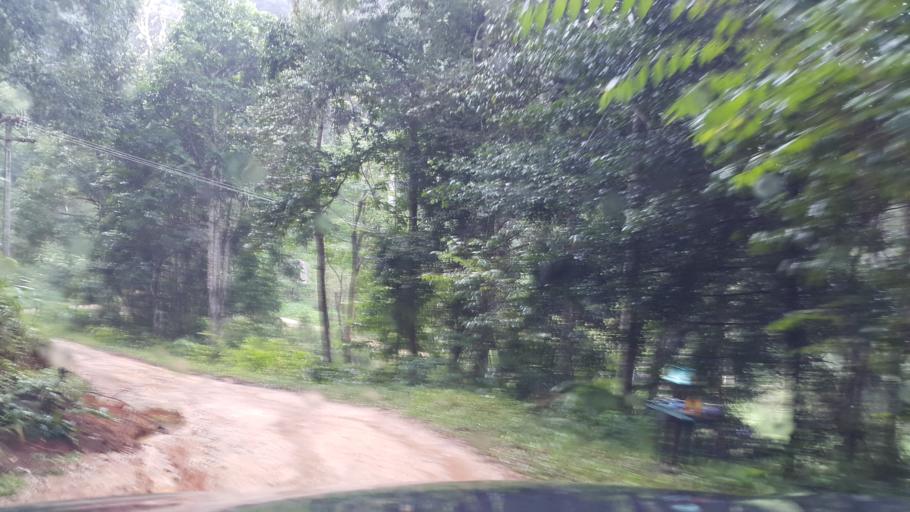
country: TH
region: Lampang
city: Wang Nuea
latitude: 19.1324
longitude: 99.3575
